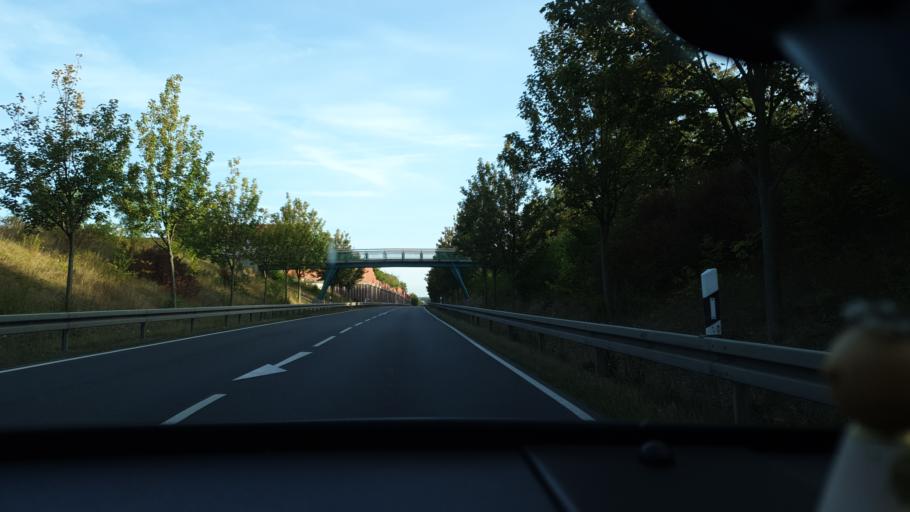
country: DE
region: Saxony
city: Eilenburg
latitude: 51.4567
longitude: 12.6116
